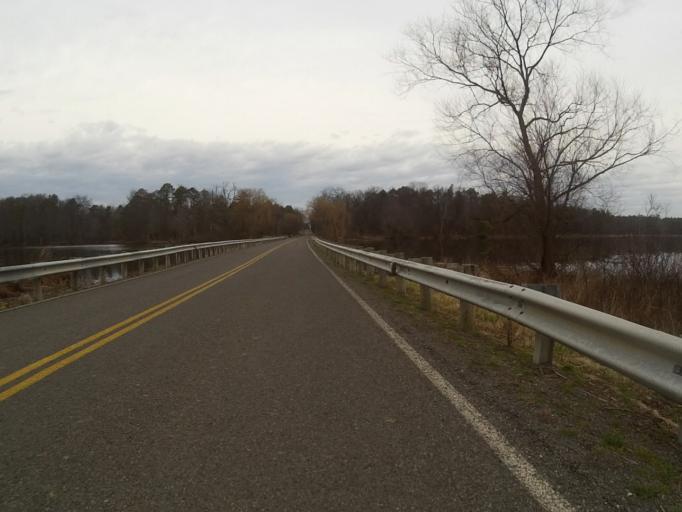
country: US
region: Ohio
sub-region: Portage County
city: Brimfield
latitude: 41.0611
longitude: -81.3288
